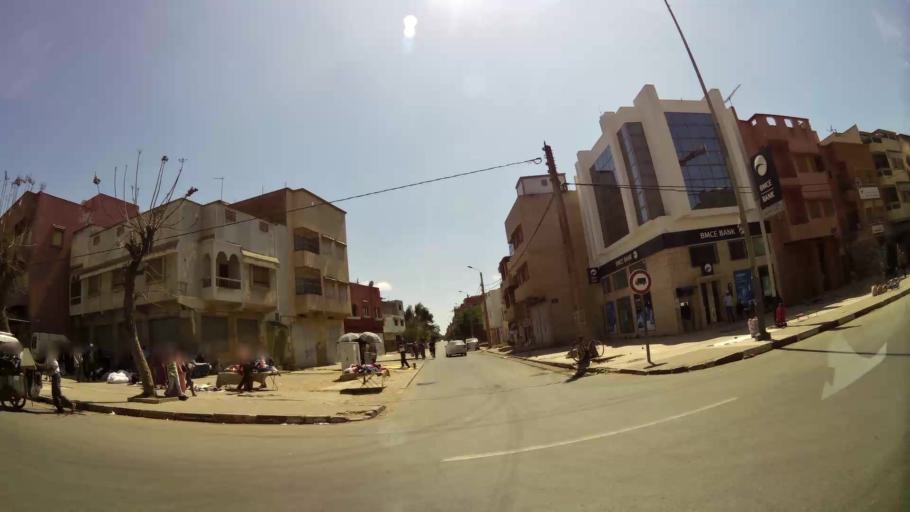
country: MA
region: Gharb-Chrarda-Beni Hssen
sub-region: Kenitra Province
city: Kenitra
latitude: 34.2424
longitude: -6.5494
